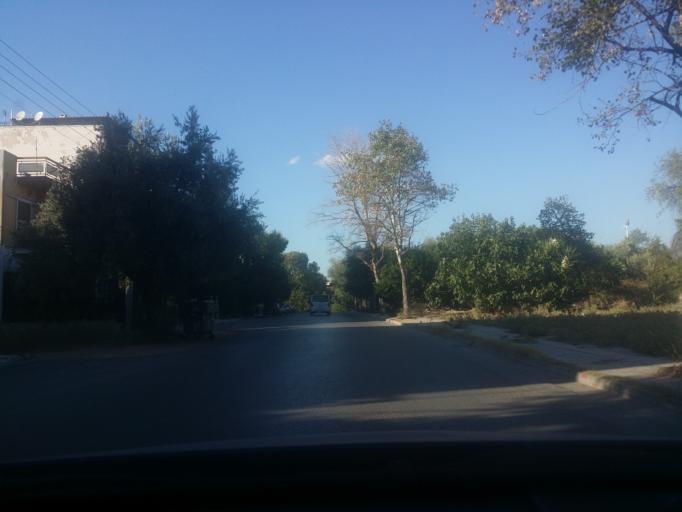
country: GR
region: Attica
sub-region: Nomarchia Athinas
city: Khalandrion
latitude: 38.0118
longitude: 23.8023
